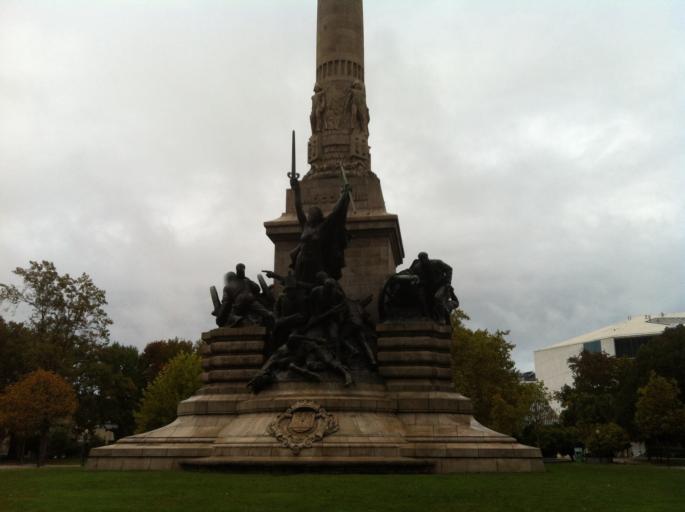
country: PT
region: Porto
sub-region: Porto
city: Porto
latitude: 41.1579
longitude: -8.6288
